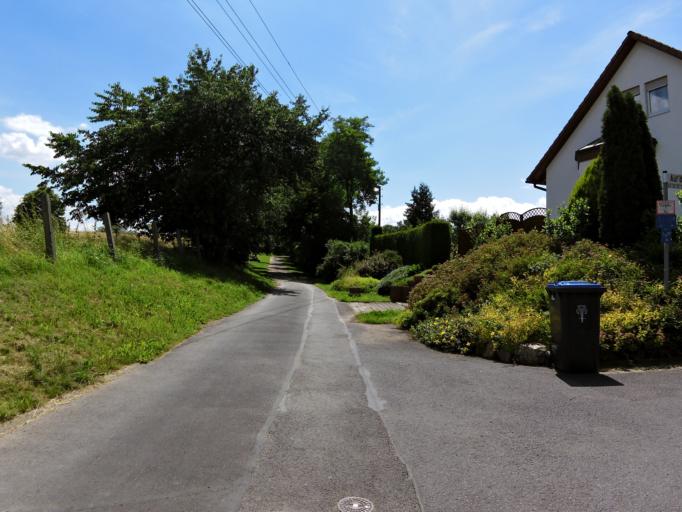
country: DE
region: Thuringia
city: Lauchroden
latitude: 50.9900
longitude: 10.1521
